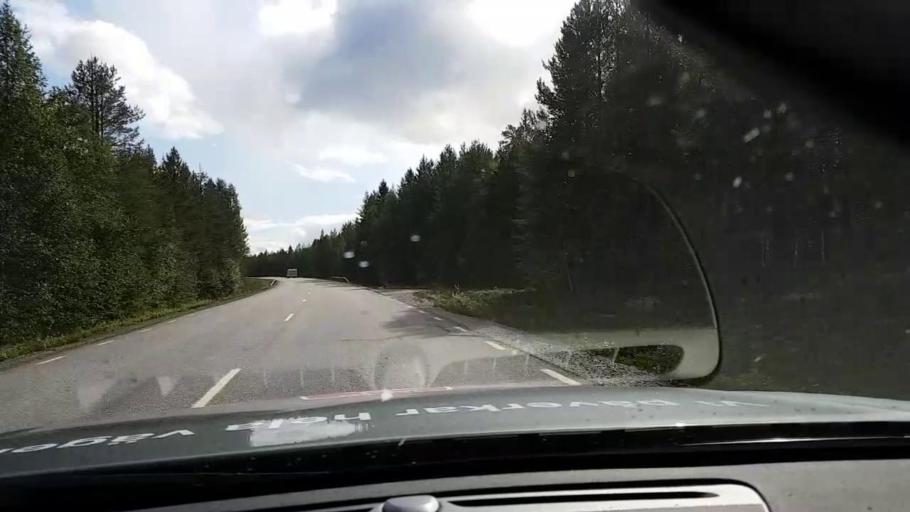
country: SE
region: Vaesternorrland
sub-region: OErnskoeldsviks Kommun
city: Bredbyn
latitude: 63.6248
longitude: 17.9078
